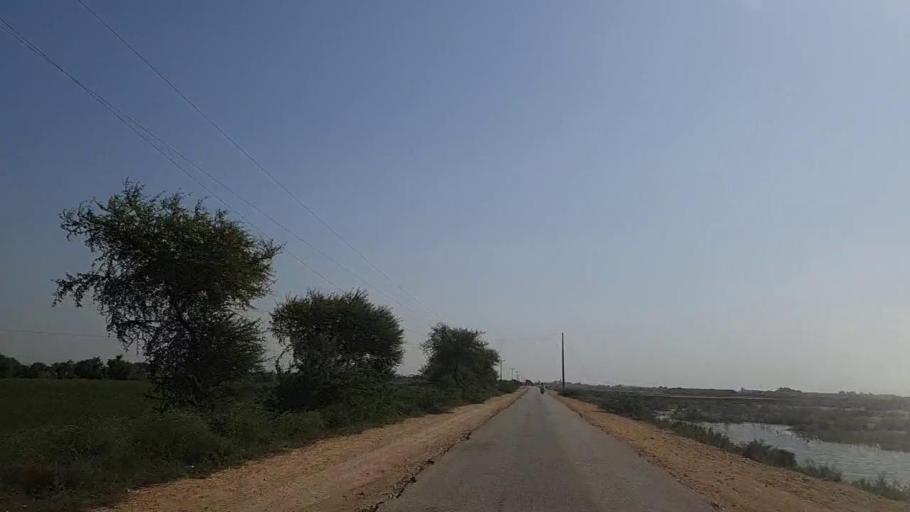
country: PK
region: Sindh
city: Mirpur Batoro
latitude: 24.6330
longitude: 68.2926
